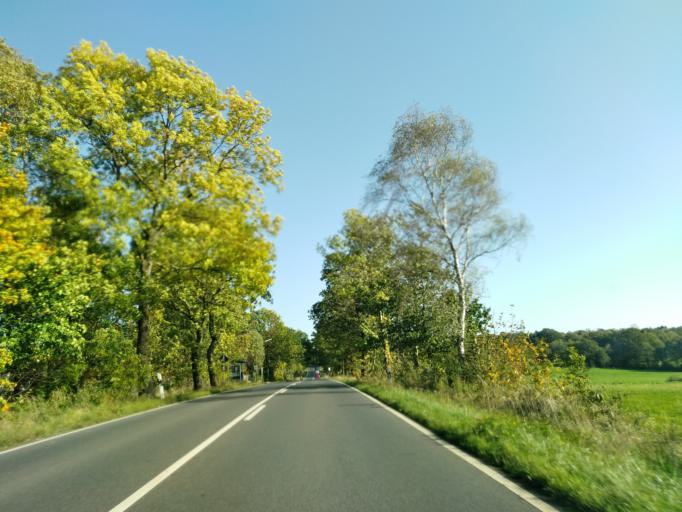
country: DE
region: Rheinland-Pfalz
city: Asbach
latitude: 50.7204
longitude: 7.3840
